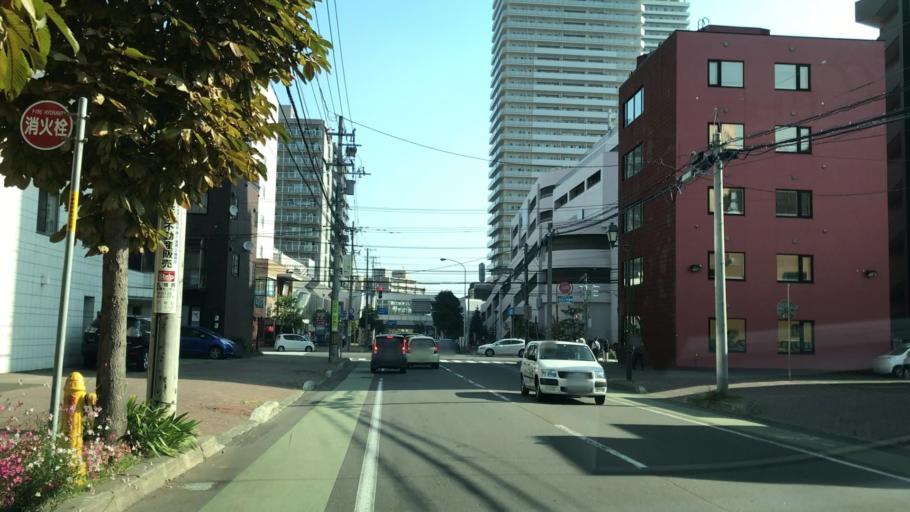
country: JP
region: Hokkaido
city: Sapporo
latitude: 43.0802
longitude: 141.3044
